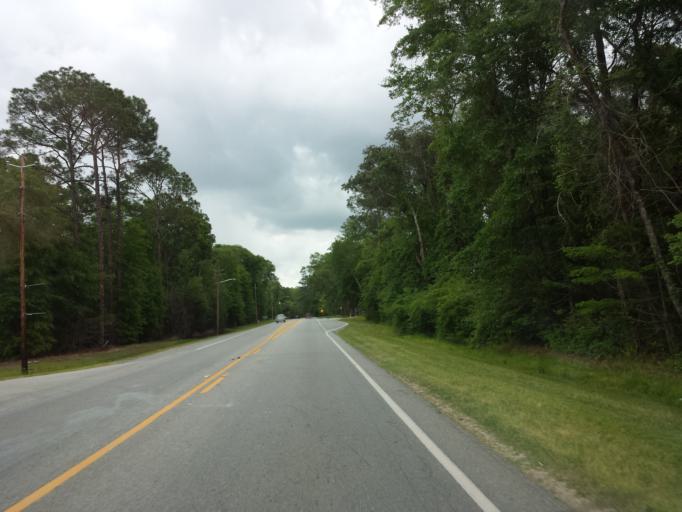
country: US
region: Georgia
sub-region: Lowndes County
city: Hahira
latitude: 30.9911
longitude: -83.3840
